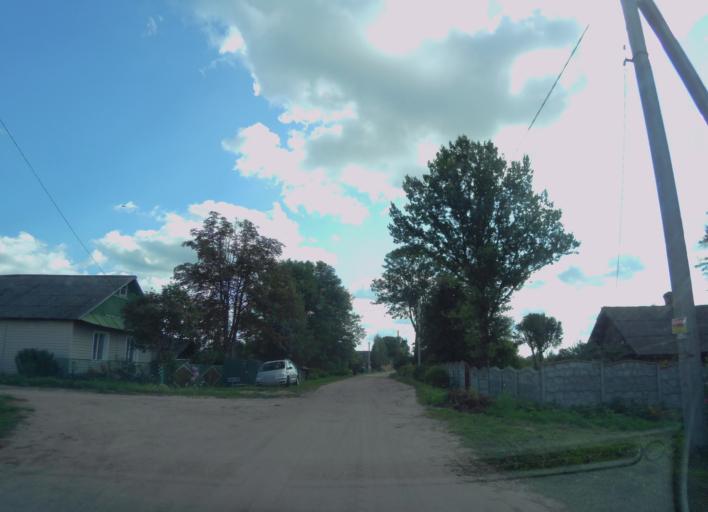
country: BY
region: Minsk
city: Zyembin
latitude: 54.3765
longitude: 28.3752
